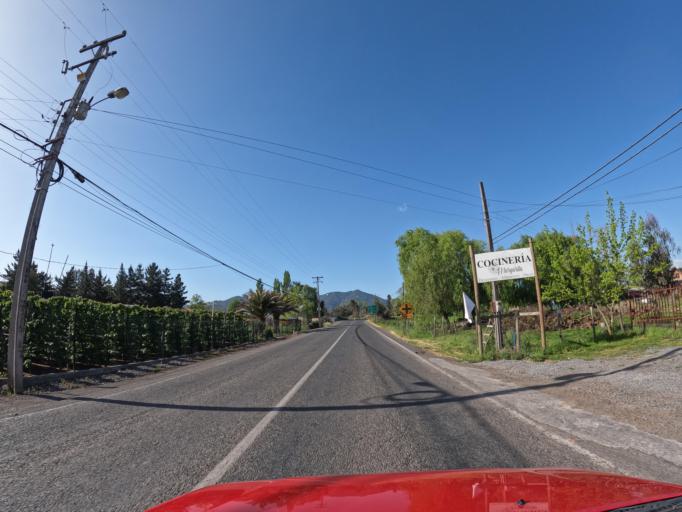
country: CL
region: Maule
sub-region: Provincia de Curico
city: Rauco
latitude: -34.8696
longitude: -71.2649
